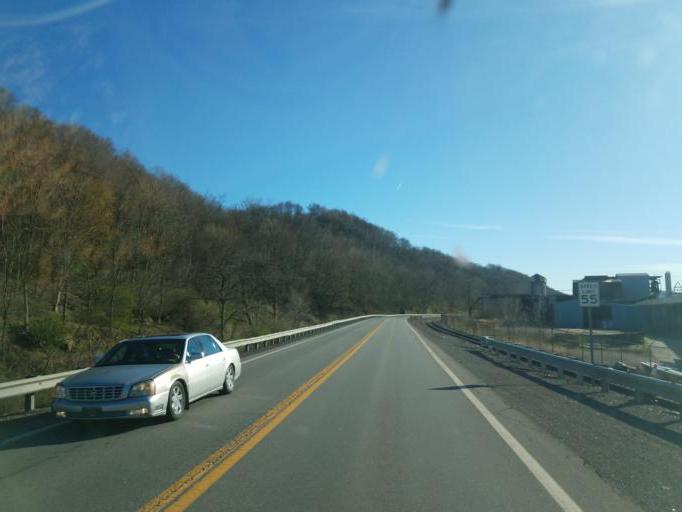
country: US
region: West Virginia
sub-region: Hancock County
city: Newell
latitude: 40.6140
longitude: -80.6206
